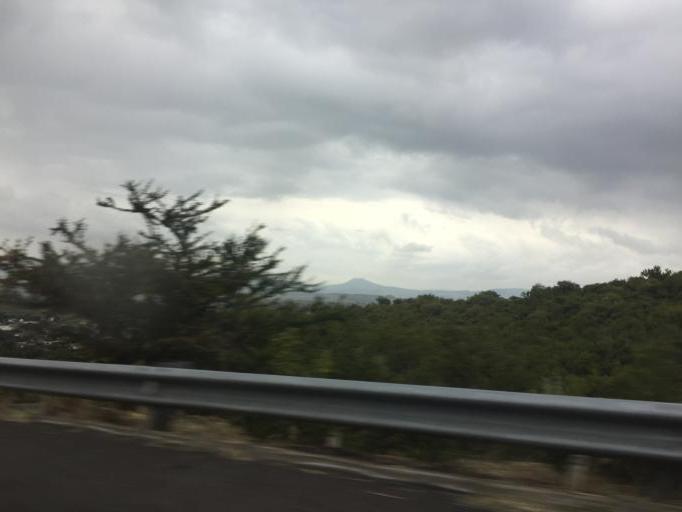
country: MX
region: Jalisco
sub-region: Zapotlan del Rey
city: Zapotlan del Rey
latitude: 20.4748
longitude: -102.9269
